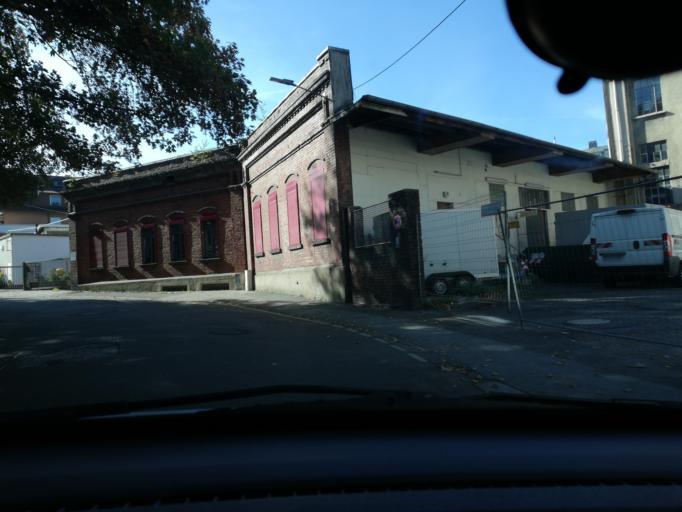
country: DE
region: North Rhine-Westphalia
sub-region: Regierungsbezirk Dusseldorf
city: Wuppertal
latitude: 51.2767
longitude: 7.1982
